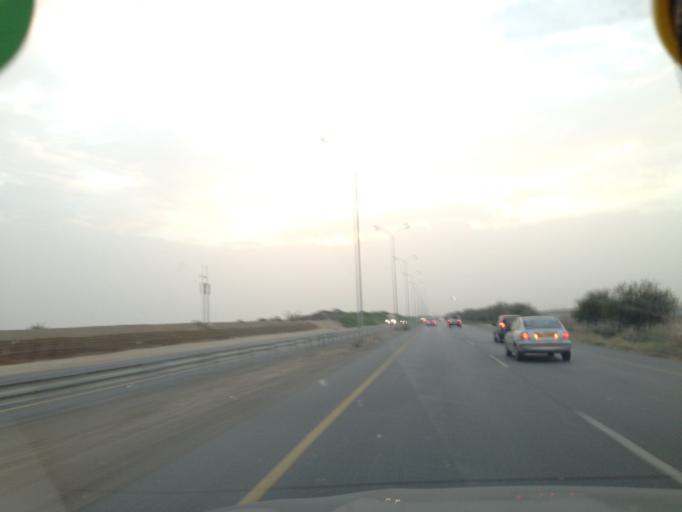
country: OM
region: Muhafazat Masqat
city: As Sib al Jadidah
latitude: 23.6170
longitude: 58.2836
